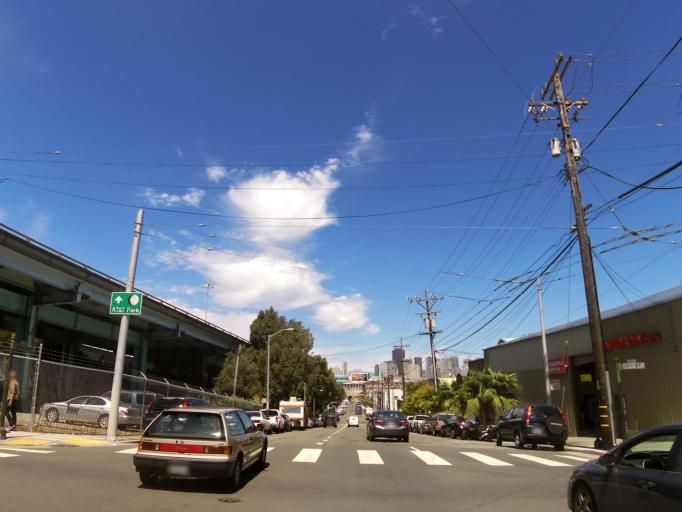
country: US
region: California
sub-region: San Francisco County
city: San Francisco
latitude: 37.7646
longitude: -122.4045
